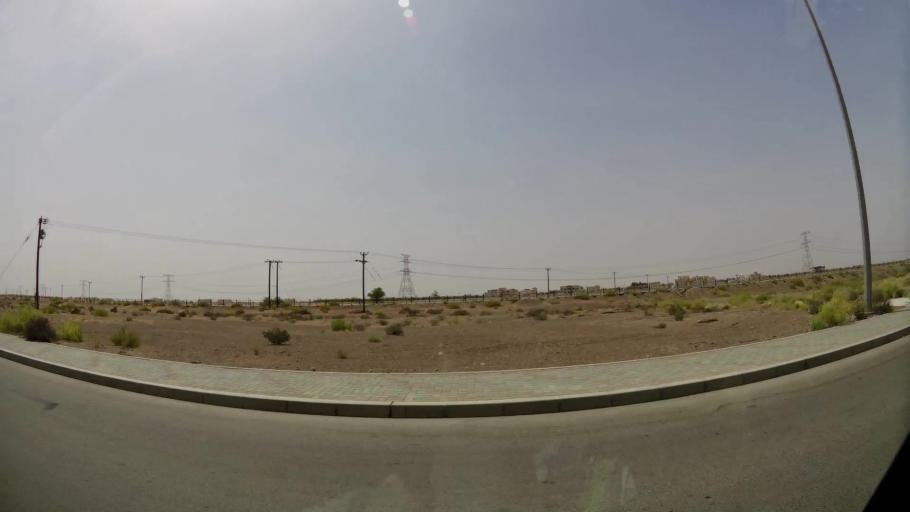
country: AE
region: Abu Dhabi
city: Al Ain
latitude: 24.1539
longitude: 55.6489
